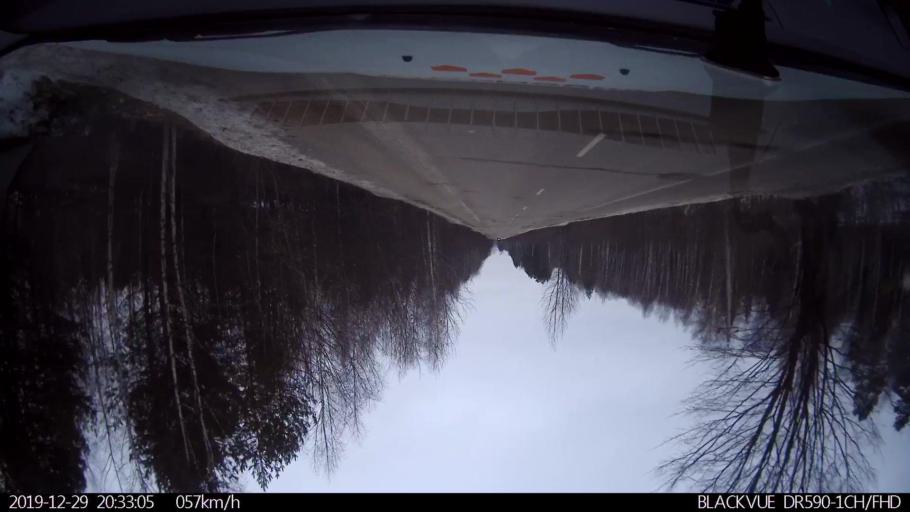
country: RU
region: Nizjnij Novgorod
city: Afonino
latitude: 56.1786
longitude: 44.0562
